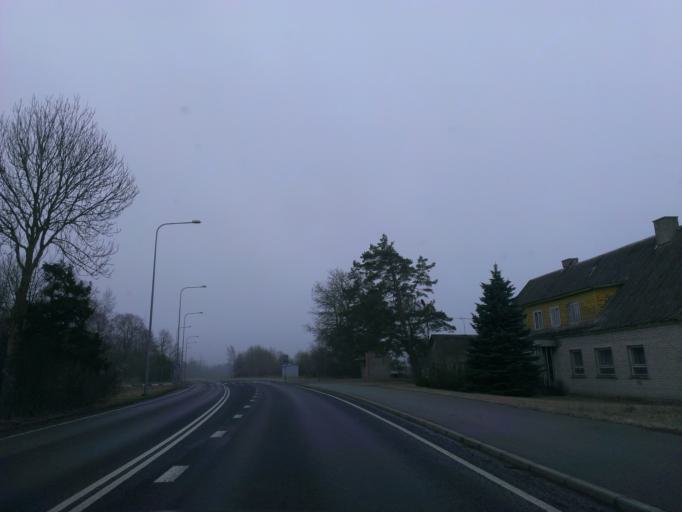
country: EE
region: Laeaene
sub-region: Lihula vald
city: Lihula
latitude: 58.5796
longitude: 23.5238
